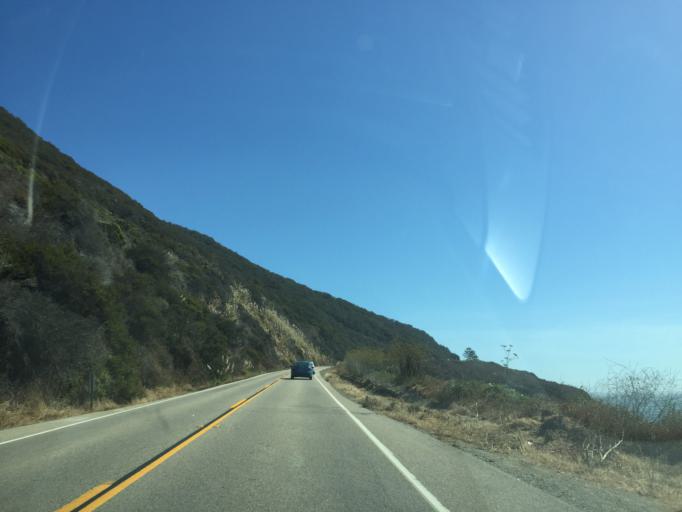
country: US
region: California
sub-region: Monterey County
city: Greenfield
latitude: 36.0420
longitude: -121.5823
